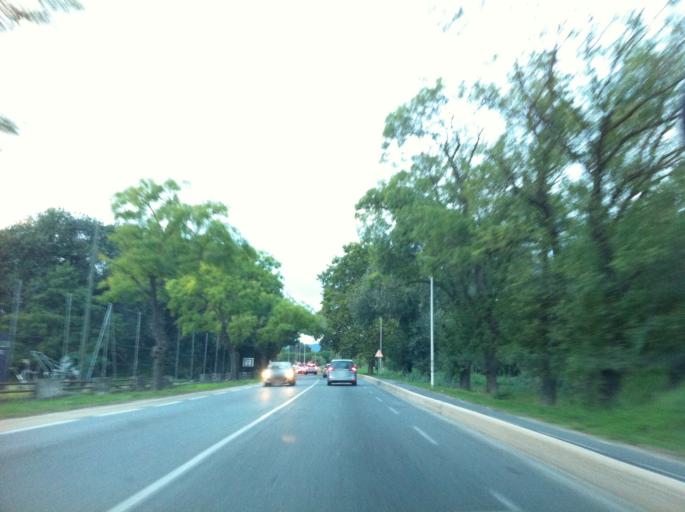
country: FR
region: Provence-Alpes-Cote d'Azur
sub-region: Departement du Var
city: Gassin
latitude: 43.2603
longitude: 6.5898
